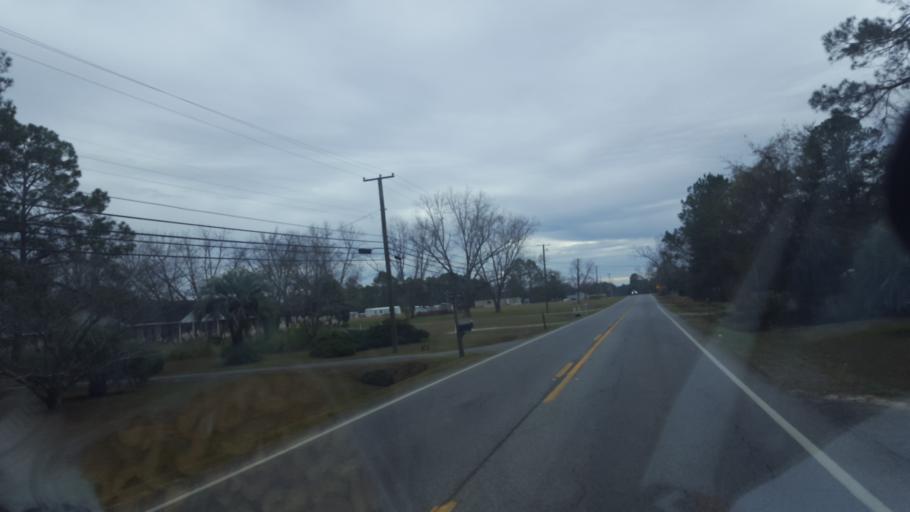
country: US
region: Georgia
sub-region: Ben Hill County
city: Fitzgerald
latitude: 31.7353
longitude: -83.2609
